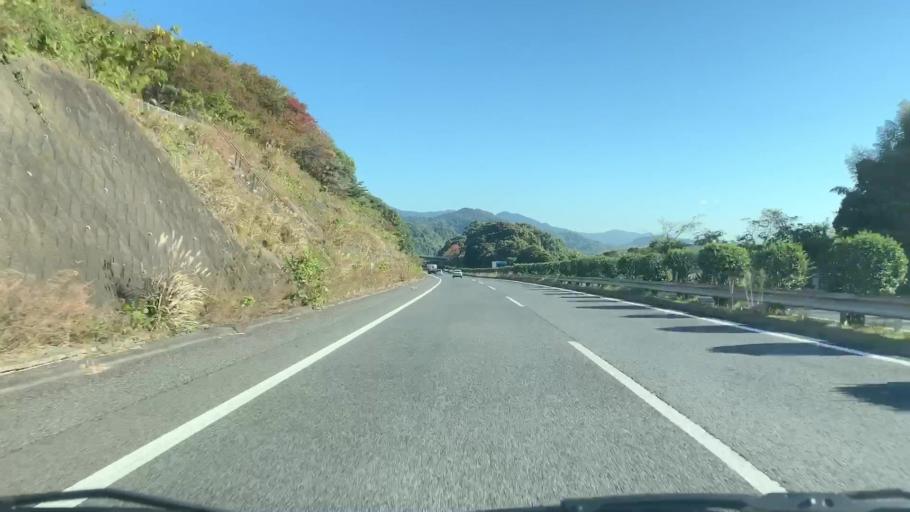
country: JP
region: Saga Prefecture
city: Saga-shi
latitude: 33.2892
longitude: 130.1630
